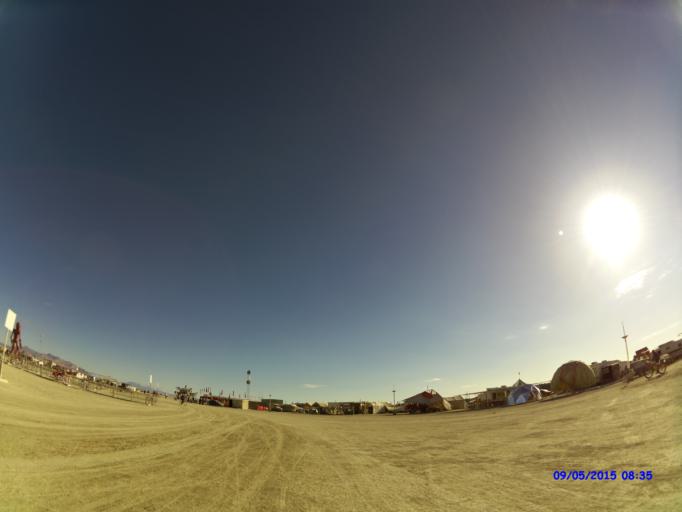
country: US
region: Nevada
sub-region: Pershing County
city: Lovelock
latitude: 40.7803
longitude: -119.2134
